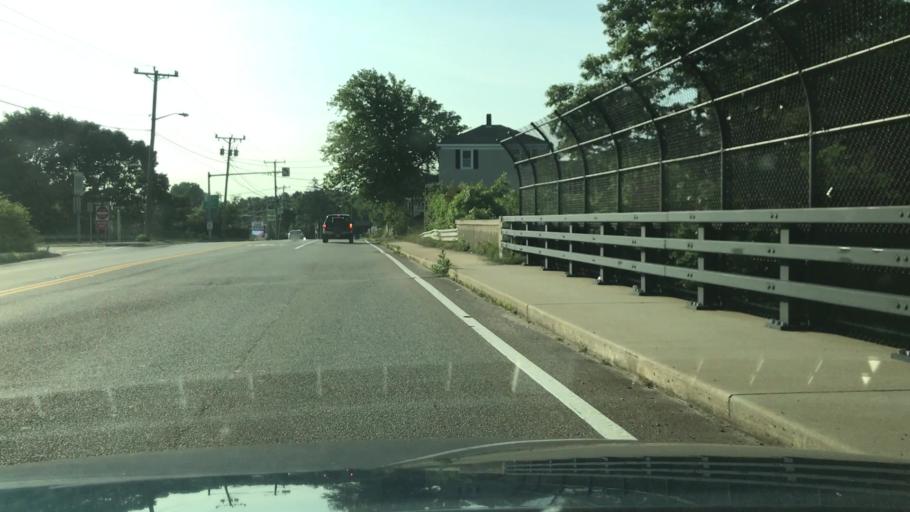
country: US
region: Massachusetts
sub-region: Plymouth County
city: Kingston
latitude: 41.9884
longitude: -70.7180
